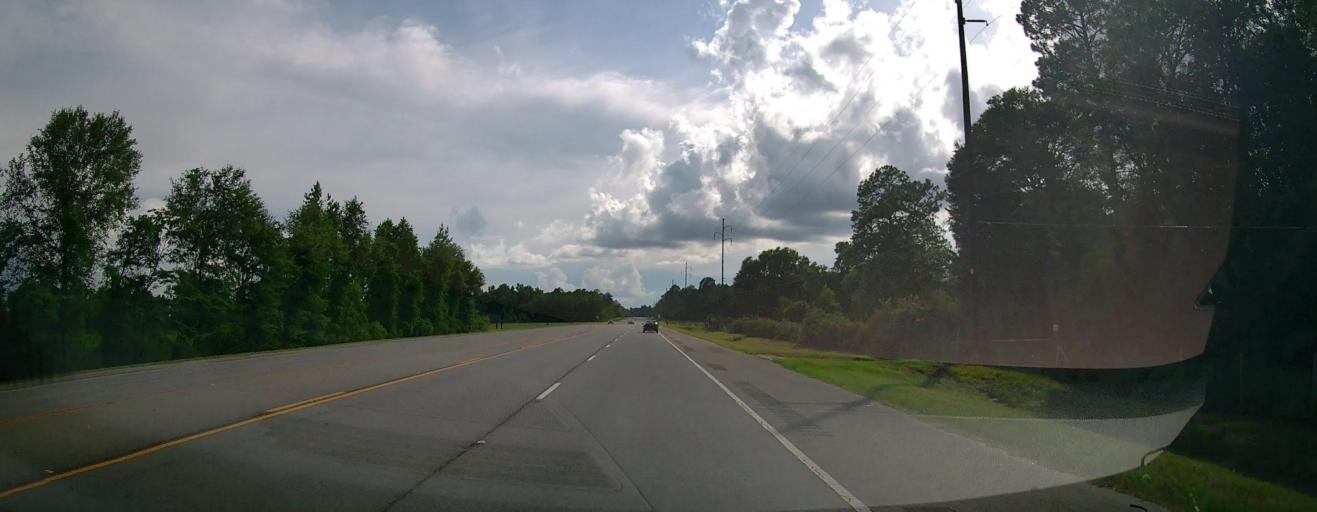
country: US
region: Georgia
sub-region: Wayne County
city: Jesup
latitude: 31.5980
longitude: -81.9358
